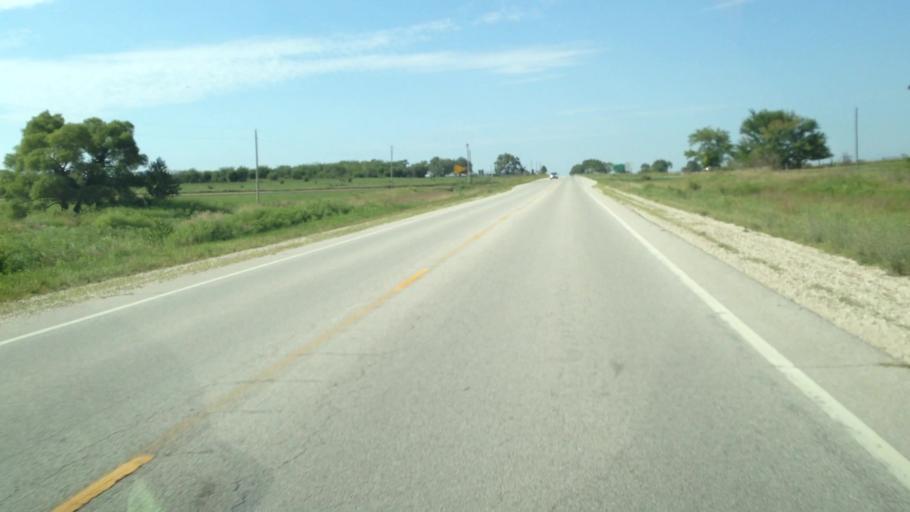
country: US
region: Kansas
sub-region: Neosho County
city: Erie
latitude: 37.4691
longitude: -95.2694
